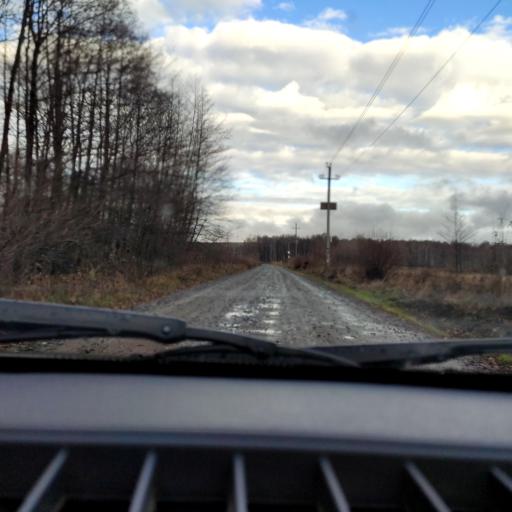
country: RU
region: Bashkortostan
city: Avdon
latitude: 54.6311
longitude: 55.7335
